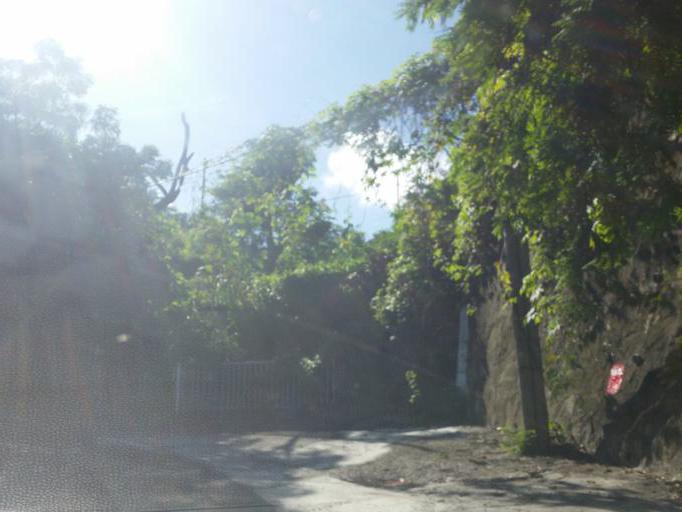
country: RE
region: Reunion
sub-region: Reunion
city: Sainte-Marie
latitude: -20.9192
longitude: 55.5162
